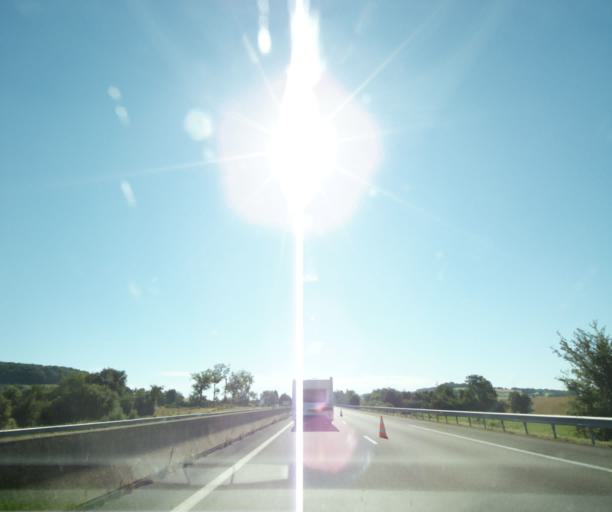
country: FR
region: Champagne-Ardenne
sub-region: Departement de la Haute-Marne
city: Rolampont
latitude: 47.9482
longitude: 5.3291
